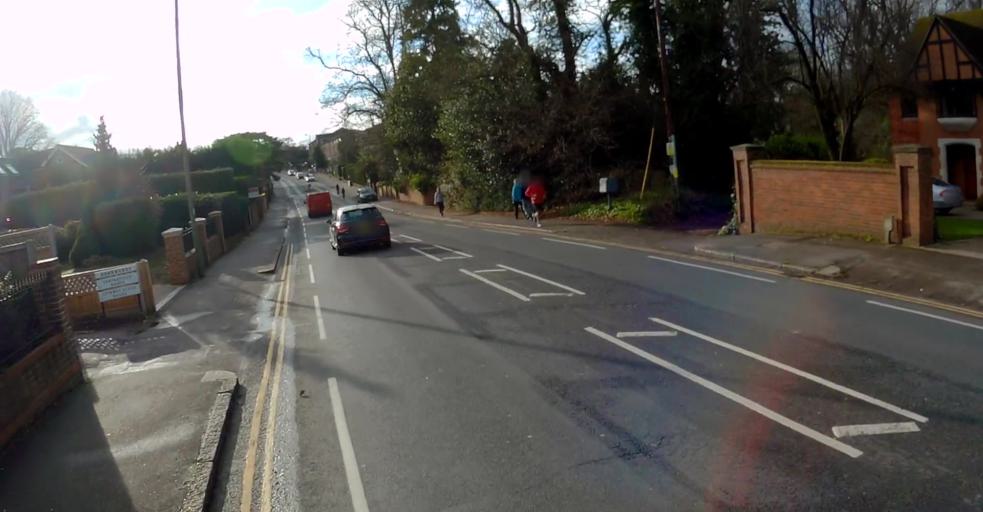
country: GB
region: England
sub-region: Surrey
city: Walton-on-Thames
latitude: 51.3837
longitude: -0.4288
